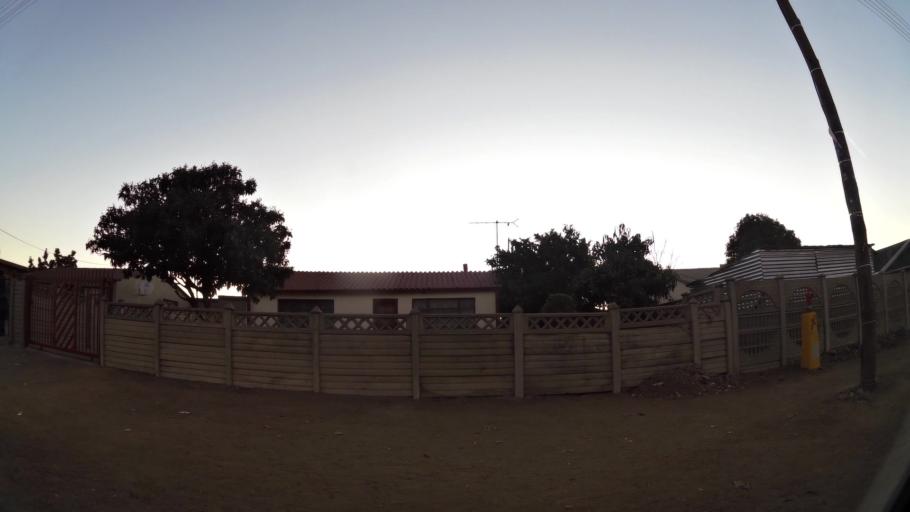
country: ZA
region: Limpopo
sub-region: Capricorn District Municipality
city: Polokwane
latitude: -23.8516
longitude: 29.3976
